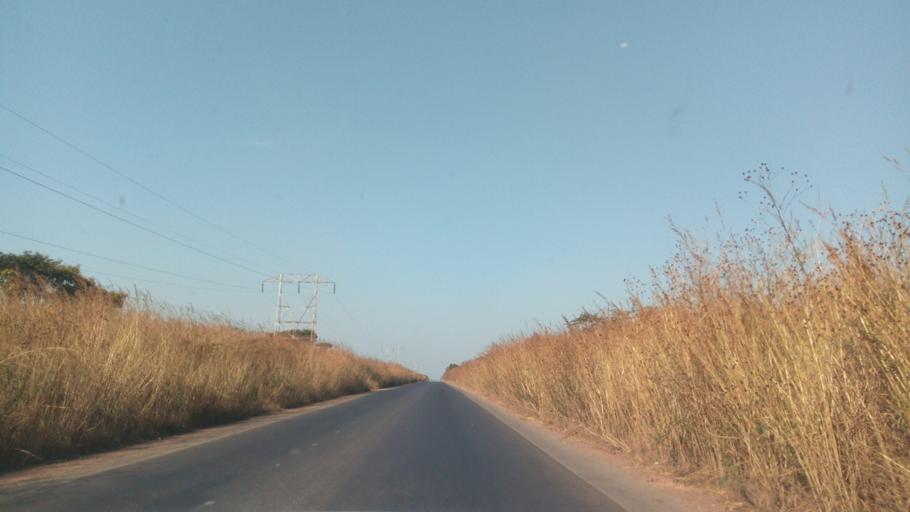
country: CD
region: Katanga
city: Likasi
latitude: -11.0015
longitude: 26.8695
